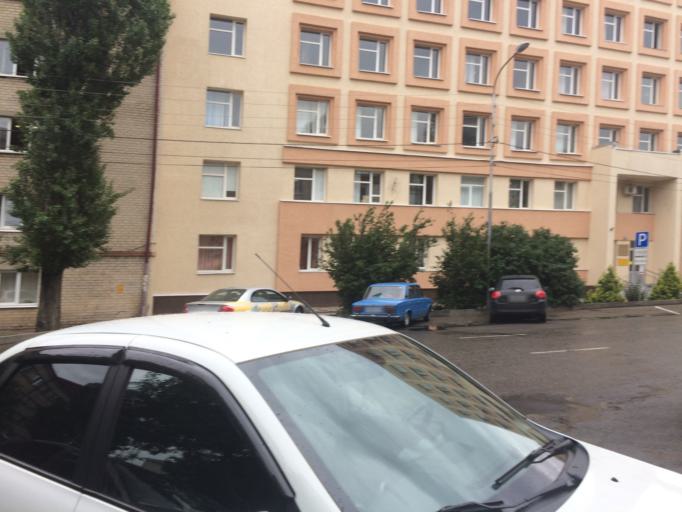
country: RU
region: Stavropol'skiy
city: Stavropol'
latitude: 45.0408
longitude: 41.9627
